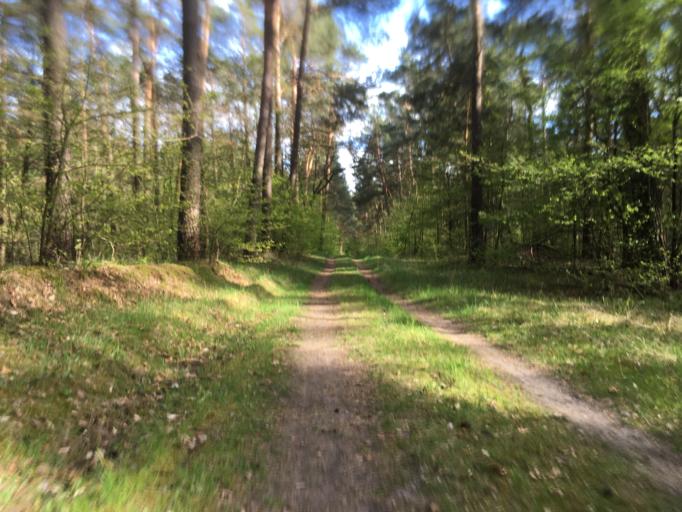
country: DE
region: Brandenburg
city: Bernau bei Berlin
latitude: 52.7114
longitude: 13.5700
